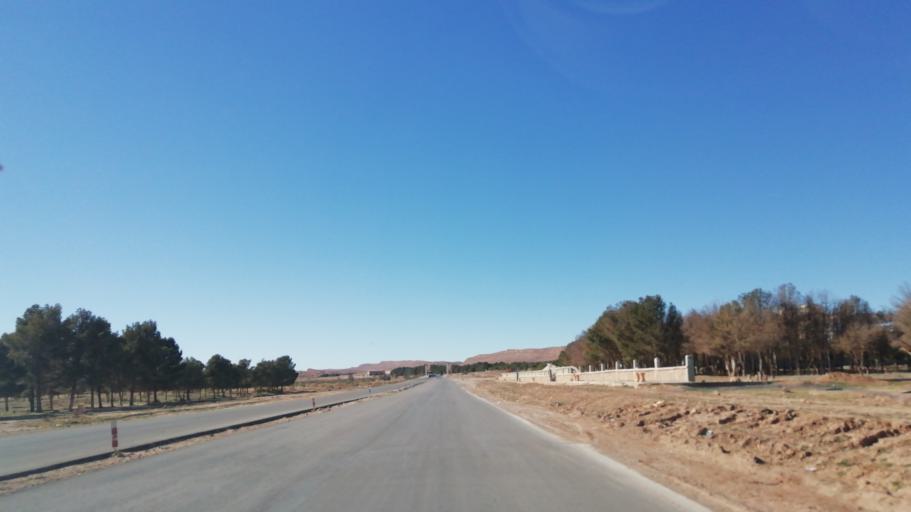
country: DZ
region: El Bayadh
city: El Bayadh
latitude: 33.7240
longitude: 1.5253
